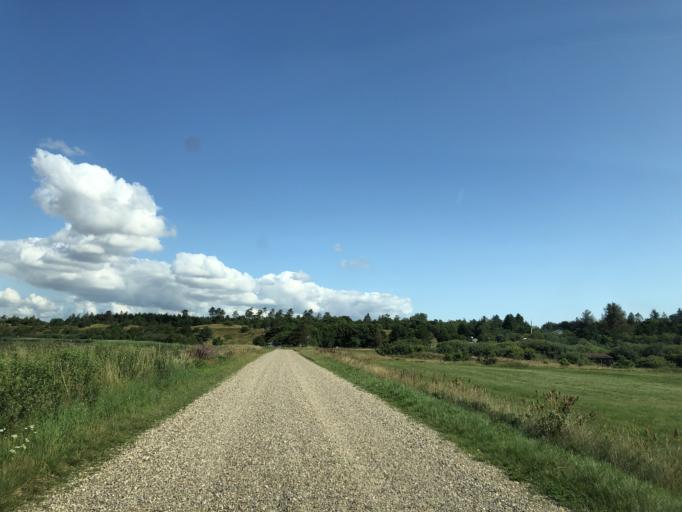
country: DK
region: Central Jutland
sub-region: Skive Kommune
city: Skive
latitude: 56.5197
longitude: 8.9564
